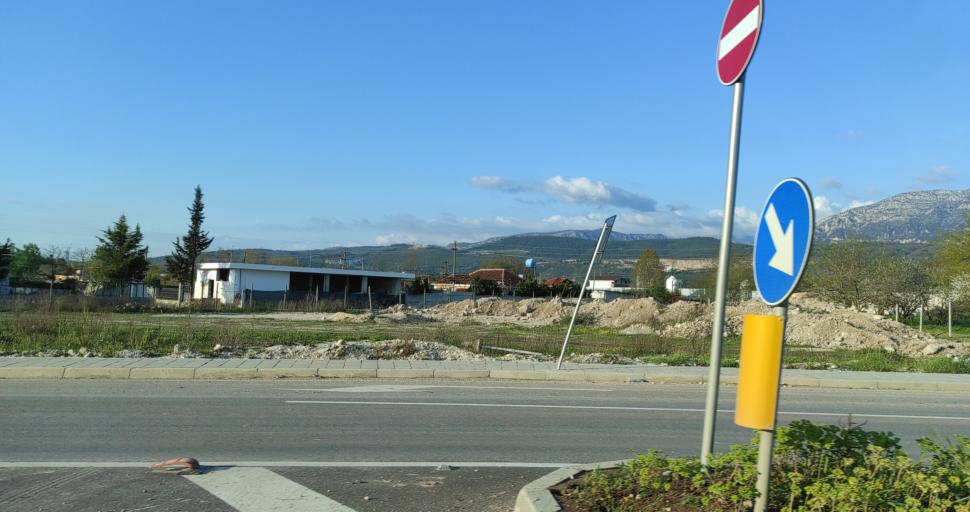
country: AL
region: Durres
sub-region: Rrethi i Krujes
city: Fushe-Kruje
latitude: 41.4867
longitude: 19.7268
